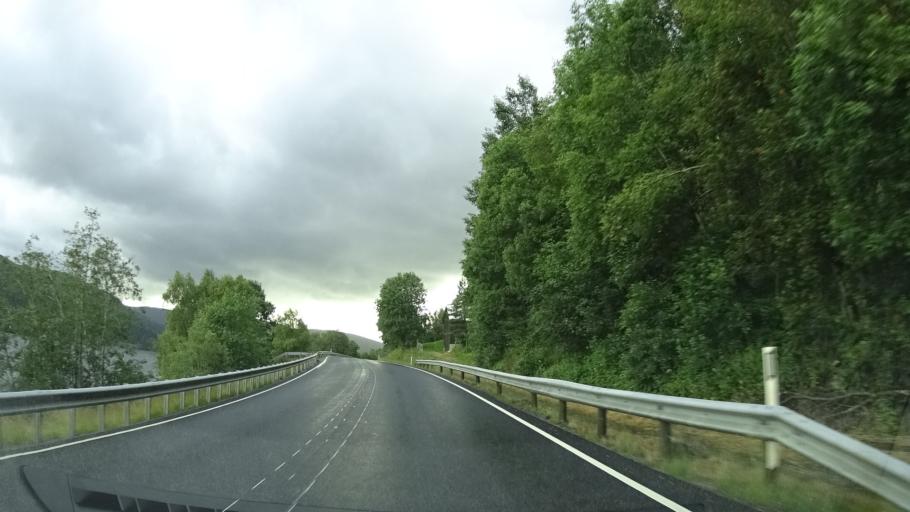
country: NO
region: Sogn og Fjordane
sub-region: Vik
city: Vik
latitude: 60.8062
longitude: 6.6326
